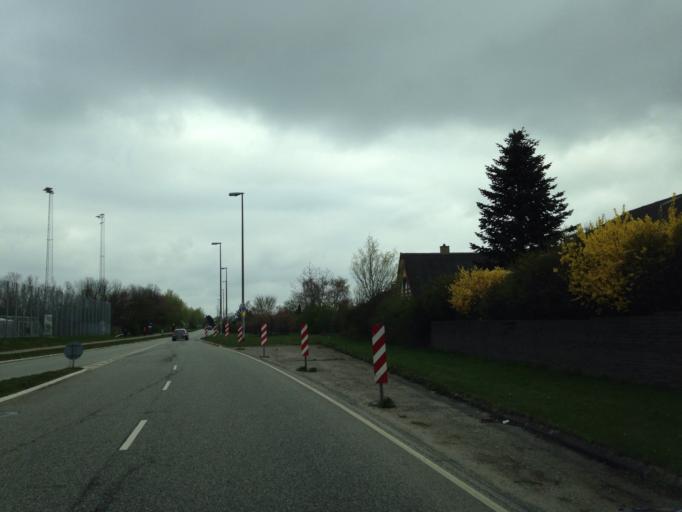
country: DK
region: Zealand
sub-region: Greve Kommune
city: Greve
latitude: 55.5927
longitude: 12.3039
